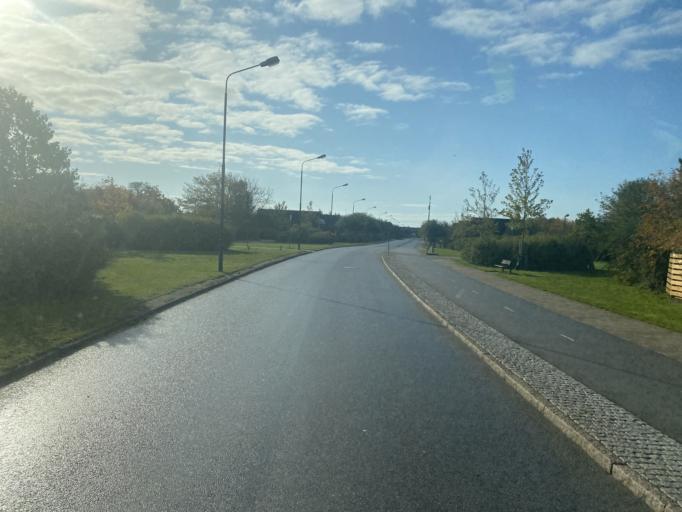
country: SE
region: Skane
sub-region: Malmo
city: Bunkeflostrand
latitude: 55.5753
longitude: 12.9636
